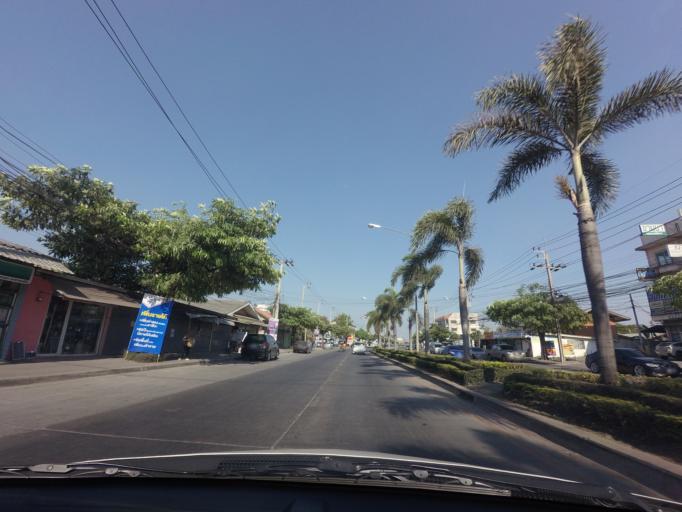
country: TH
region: Bangkok
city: Nong Chok
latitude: 13.8560
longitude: 100.8569
